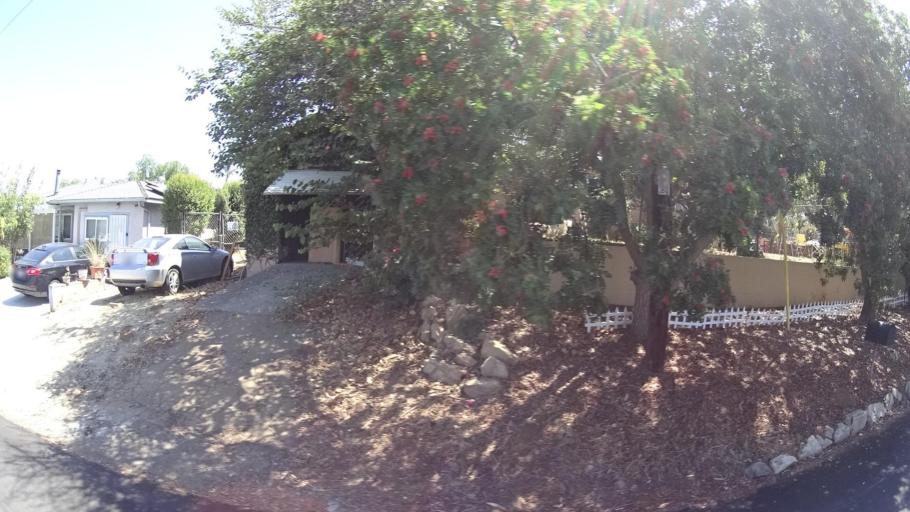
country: US
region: California
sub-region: San Diego County
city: Fallbrook
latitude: 33.3804
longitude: -117.2492
